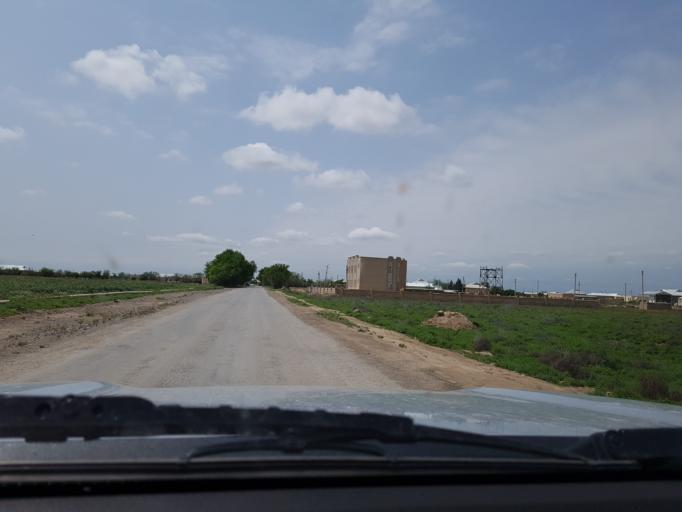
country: TM
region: Mary
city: Bayramaly
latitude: 37.6596
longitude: 62.1148
